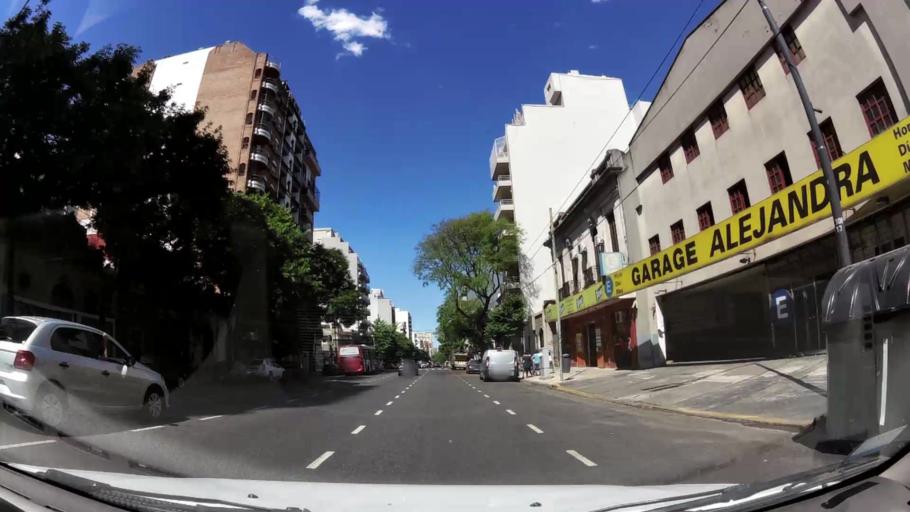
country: AR
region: Buenos Aires F.D.
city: Villa Santa Rita
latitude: -34.6299
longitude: -58.4469
